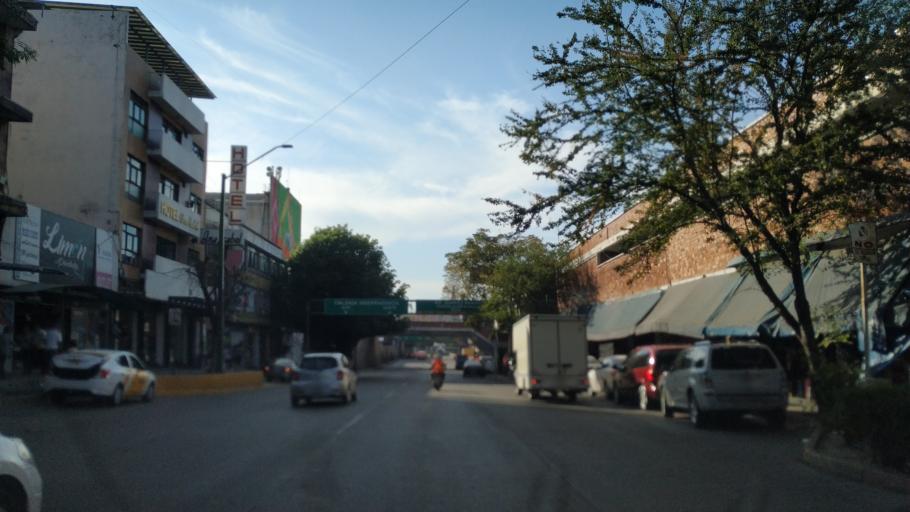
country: MX
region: Jalisco
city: Guadalajara
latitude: 20.6747
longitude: -103.3386
